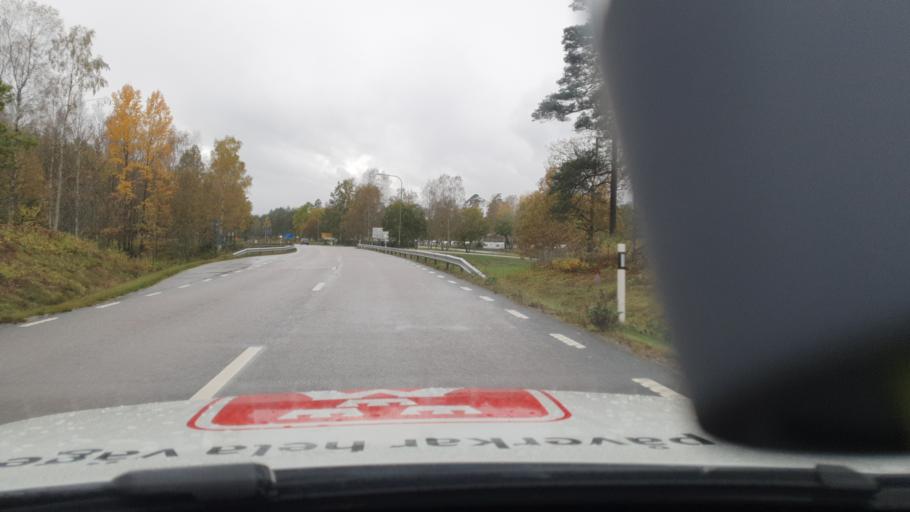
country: SE
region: Vaestra Goetaland
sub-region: Dals-Ed Kommun
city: Ed
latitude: 58.9001
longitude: 11.9397
